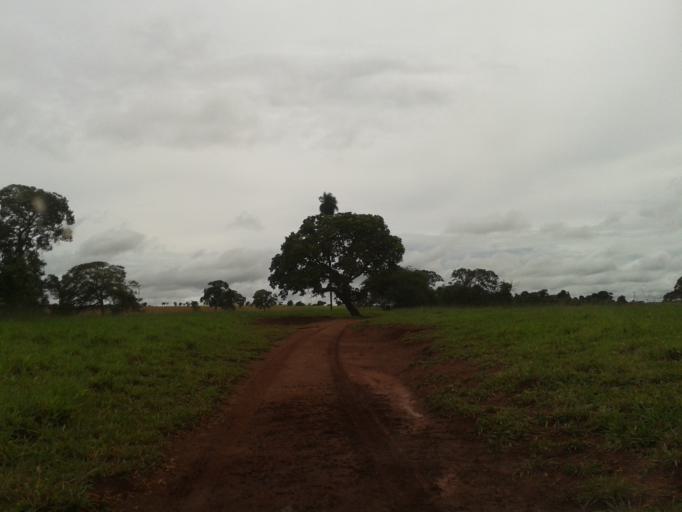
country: BR
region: Minas Gerais
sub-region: Capinopolis
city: Capinopolis
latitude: -18.7798
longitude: -49.7734
